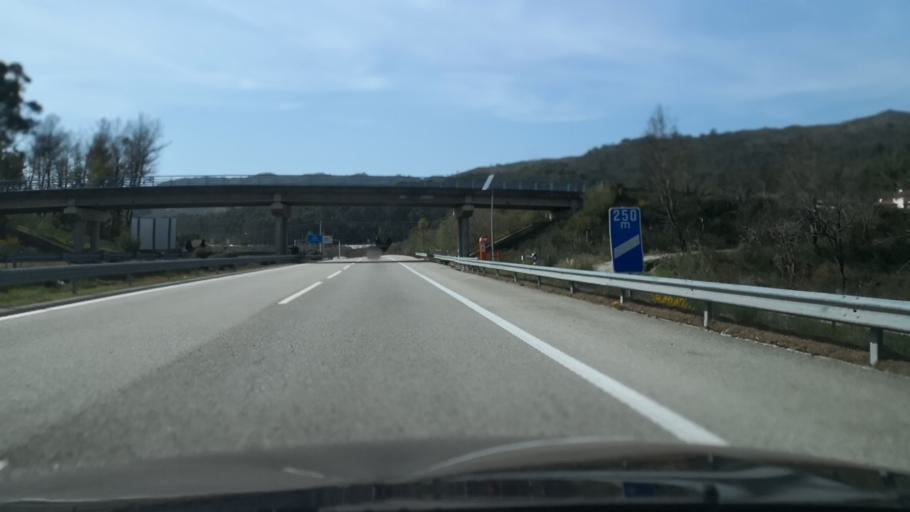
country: PT
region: Viseu
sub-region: Oliveira de Frades
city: Oliveira de Frades
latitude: 40.6877
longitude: -8.2612
